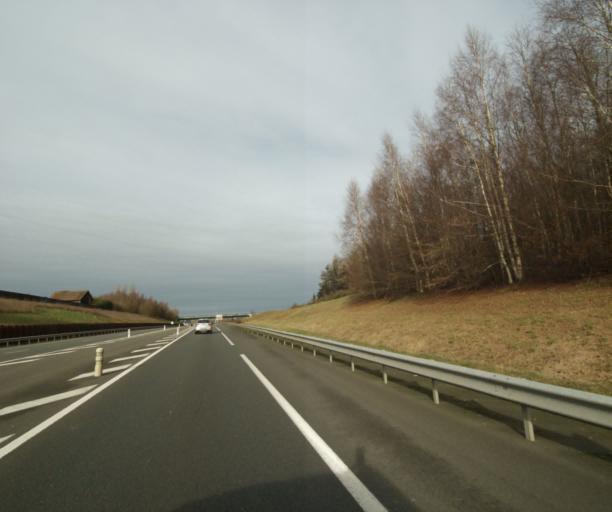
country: FR
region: Pays de la Loire
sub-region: Departement de la Sarthe
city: Sarge-les-le-Mans
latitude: 48.0142
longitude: 0.2418
